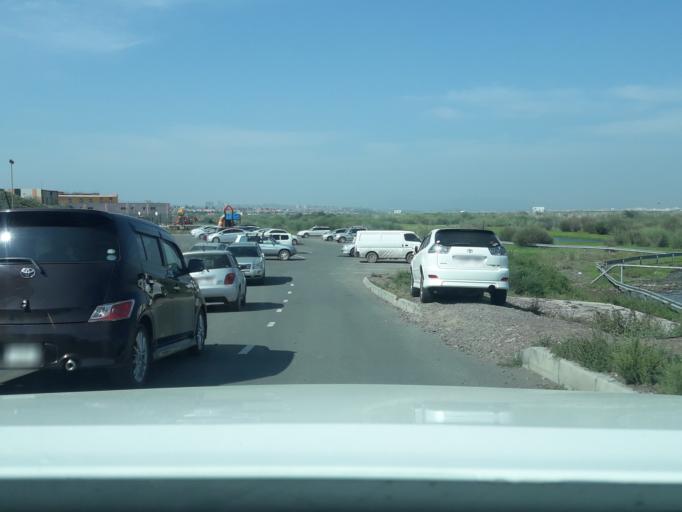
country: MN
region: Ulaanbaatar
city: Ulaanbaatar
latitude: 47.8827
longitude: 106.8535
